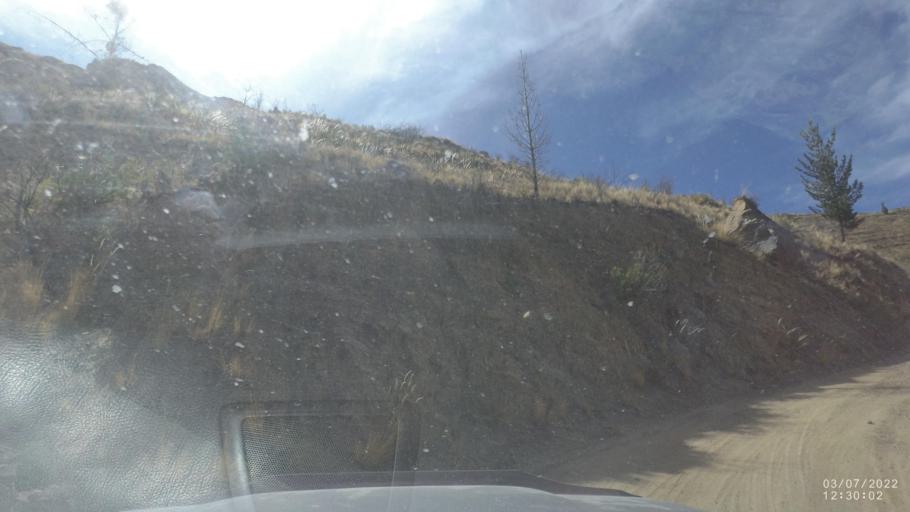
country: BO
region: Cochabamba
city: Irpa Irpa
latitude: -17.8097
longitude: -66.6097
